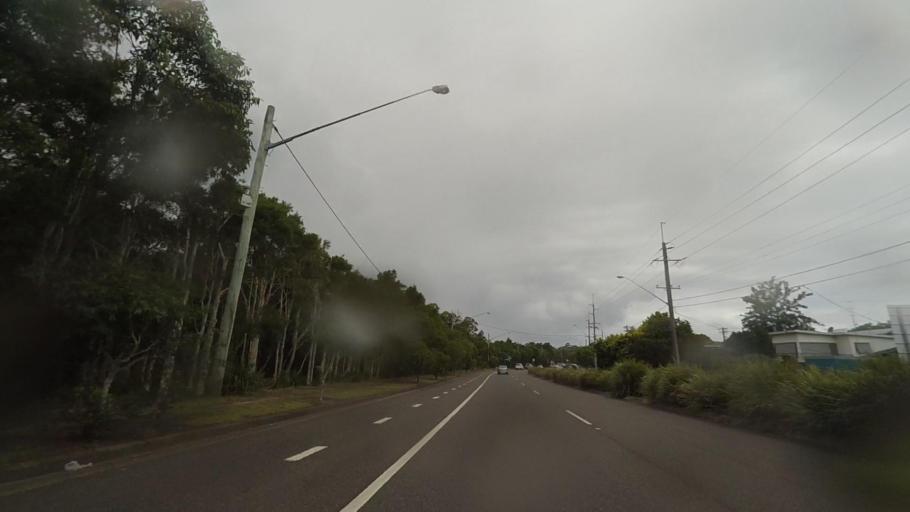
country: AU
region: New South Wales
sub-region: Wyong Shire
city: Tumbi Vmbi
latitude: -33.3631
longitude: 151.4504
